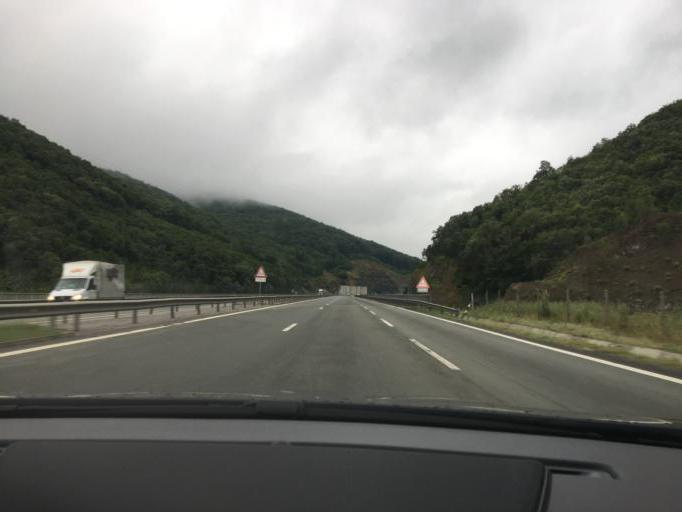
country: BG
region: Sofiya
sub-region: Obshtina Bozhurishte
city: Bozhurishte
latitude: 42.6722
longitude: 23.1507
